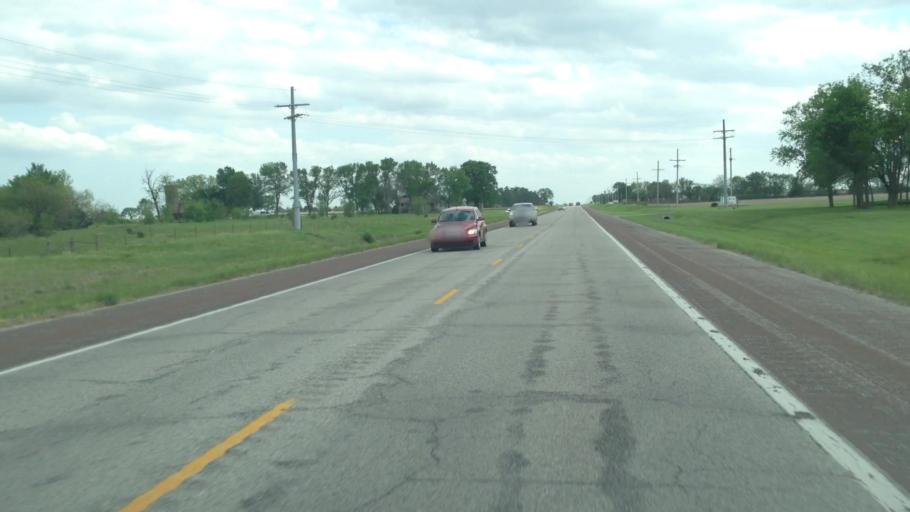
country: US
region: Kansas
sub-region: Franklin County
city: Ottawa
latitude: 38.5490
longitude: -95.2678
